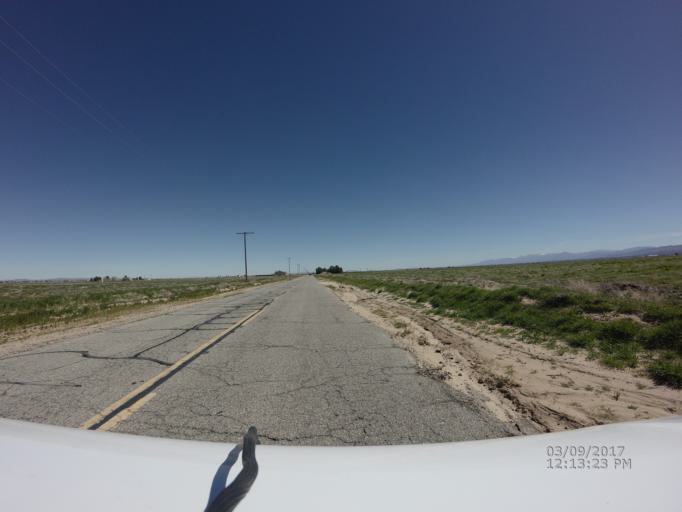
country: US
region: California
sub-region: Los Angeles County
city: Quartz Hill
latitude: 34.7329
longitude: -118.2885
